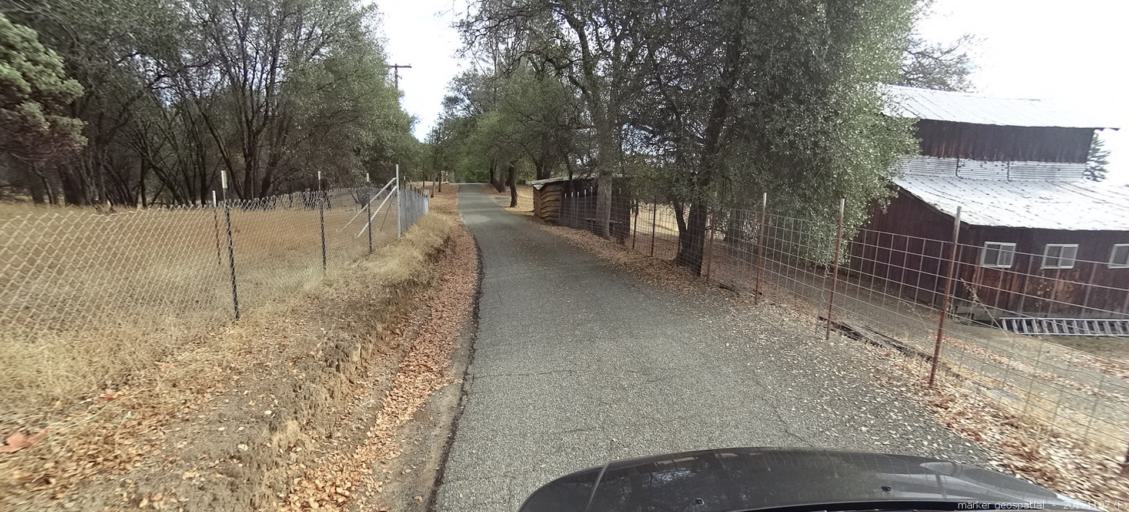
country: US
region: California
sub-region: Shasta County
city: Shasta
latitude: 40.5008
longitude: -122.5981
